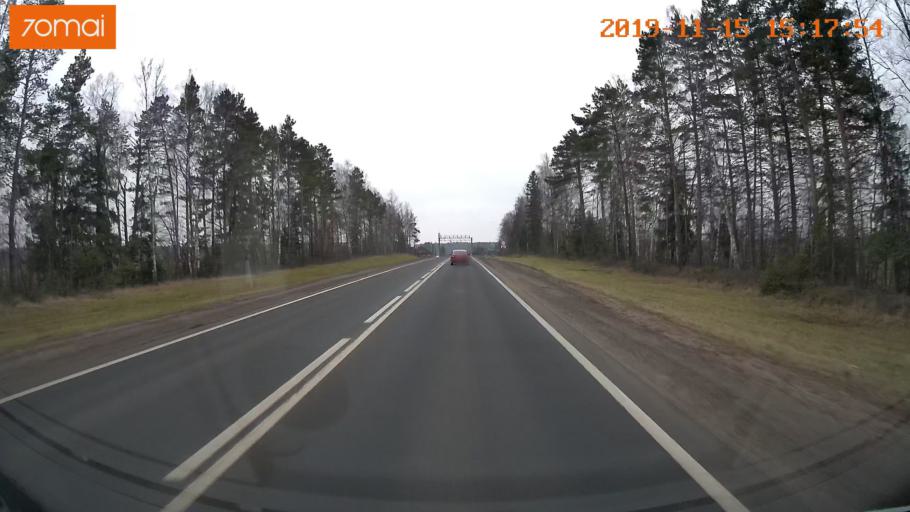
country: RU
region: Jaroslavl
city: Danilov
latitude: 58.2542
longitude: 40.1807
